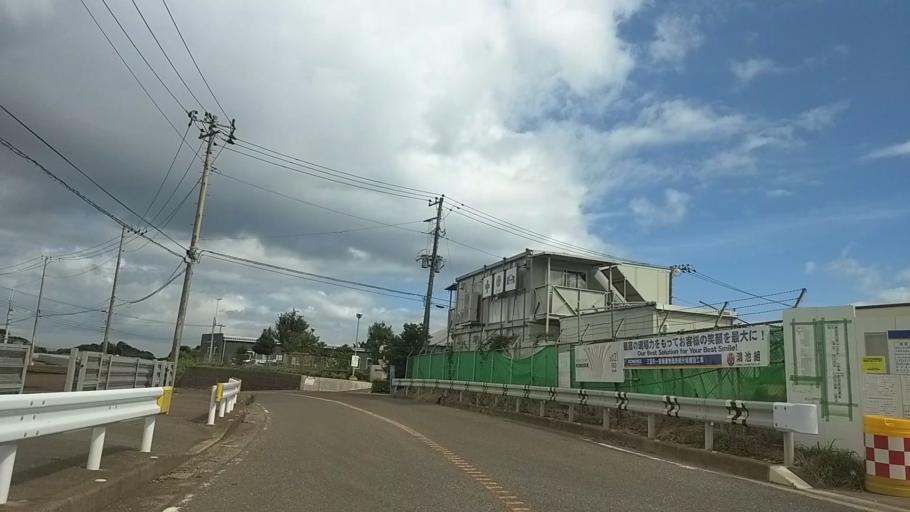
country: JP
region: Kanagawa
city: Miura
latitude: 35.1415
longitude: 139.6426
